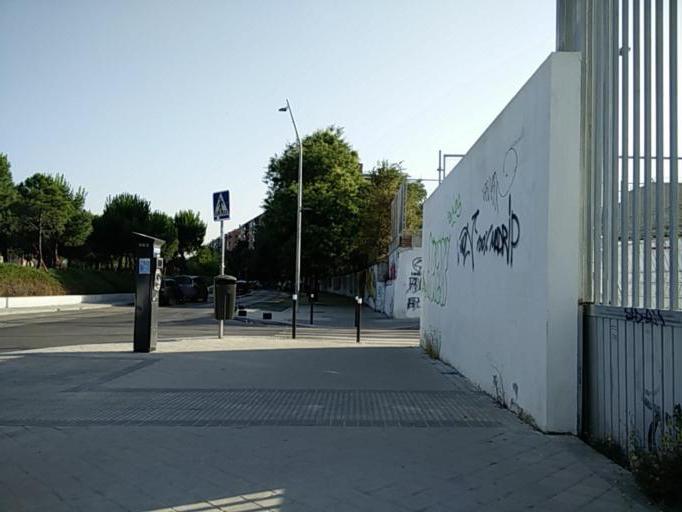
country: ES
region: Madrid
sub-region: Provincia de Madrid
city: Carabanchel
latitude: 40.4075
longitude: -3.7214
